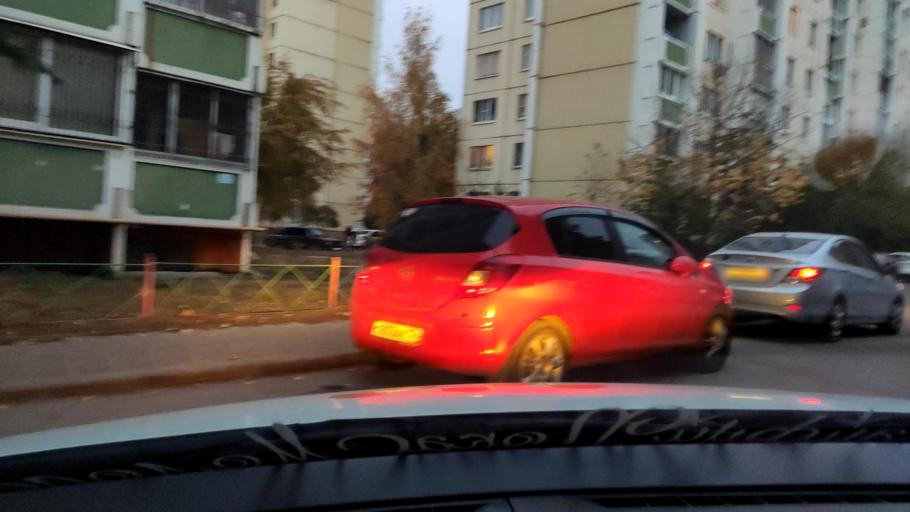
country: RU
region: Voronezj
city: Podgornoye
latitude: 51.7202
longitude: 39.1667
